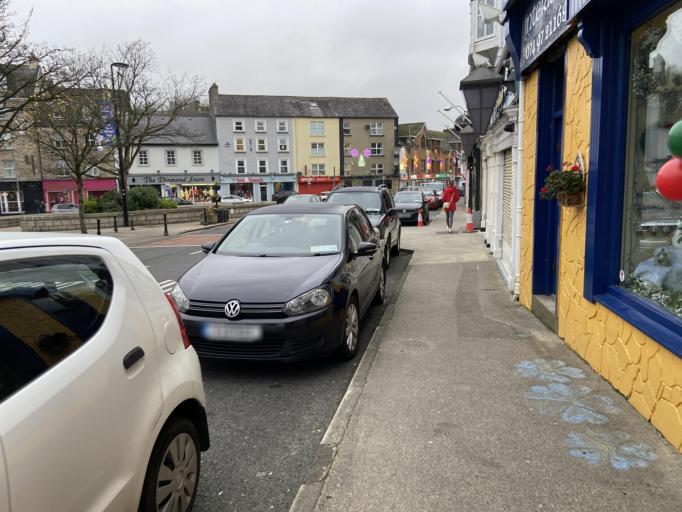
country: IE
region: Ulster
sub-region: County Donegal
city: Donegal
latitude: 54.6540
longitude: -8.1098
